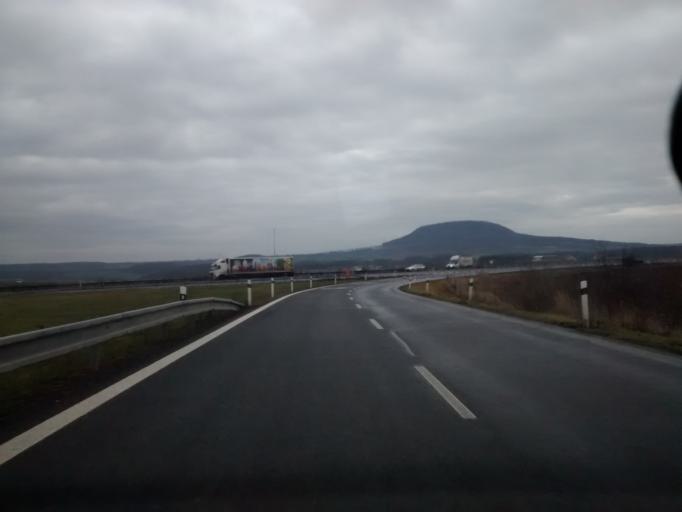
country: CZ
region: Ustecky
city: Roudnice nad Labem
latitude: 50.3931
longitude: 14.2281
